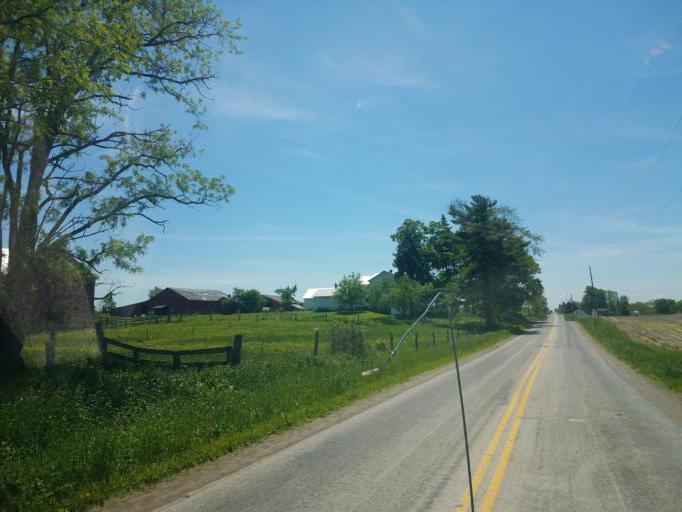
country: US
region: Ohio
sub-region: Ashland County
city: Ashland
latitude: 40.9545
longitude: -82.2437
